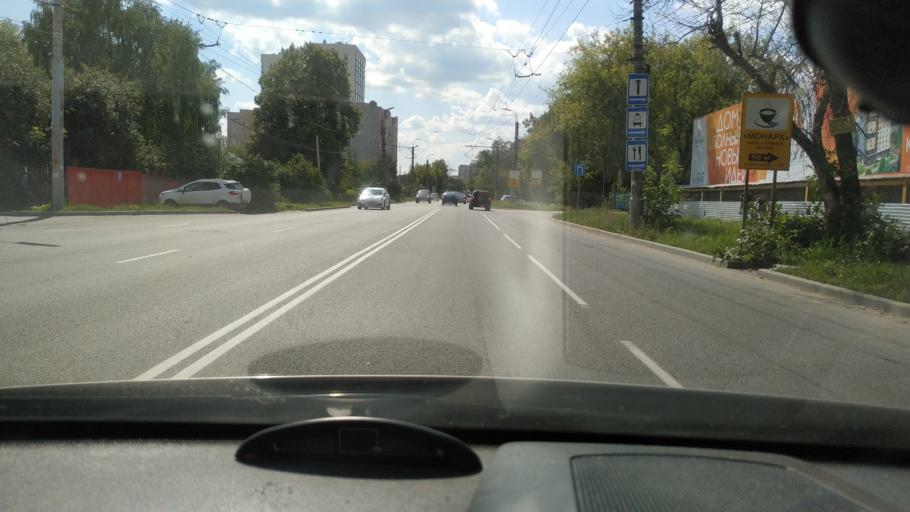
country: RU
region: Rjazan
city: Ryazan'
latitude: 54.6370
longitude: 39.6770
